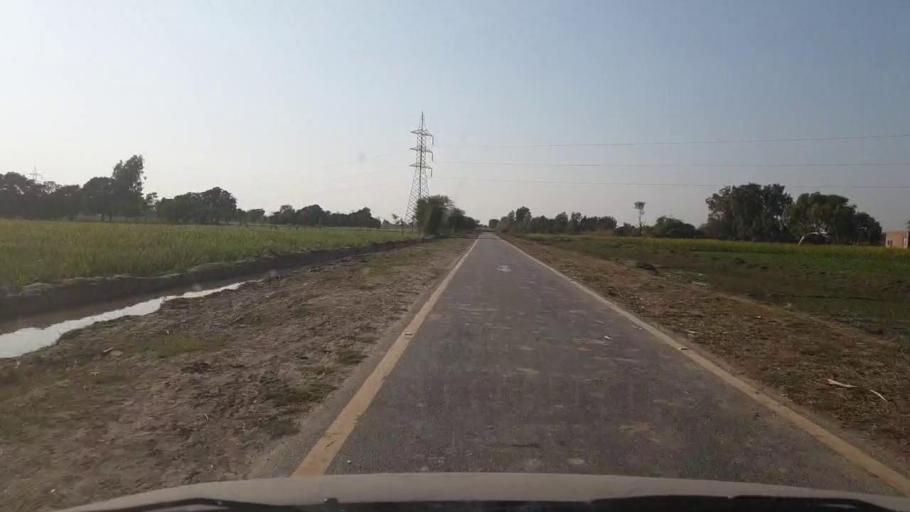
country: PK
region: Sindh
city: Samaro
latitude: 25.2870
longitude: 69.3573
